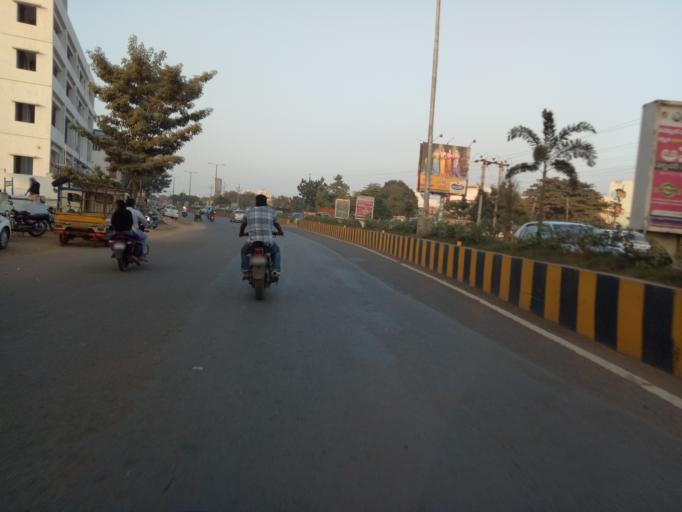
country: IN
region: Andhra Pradesh
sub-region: Nellore
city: Nellore
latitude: 14.4399
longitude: 79.9855
